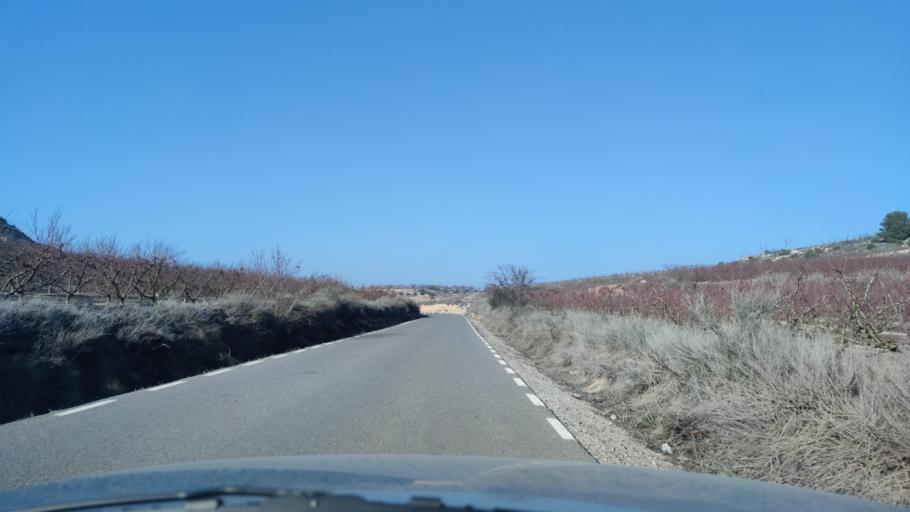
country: ES
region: Catalonia
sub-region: Provincia de Lleida
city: Sunyer
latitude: 41.5160
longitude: 0.5662
